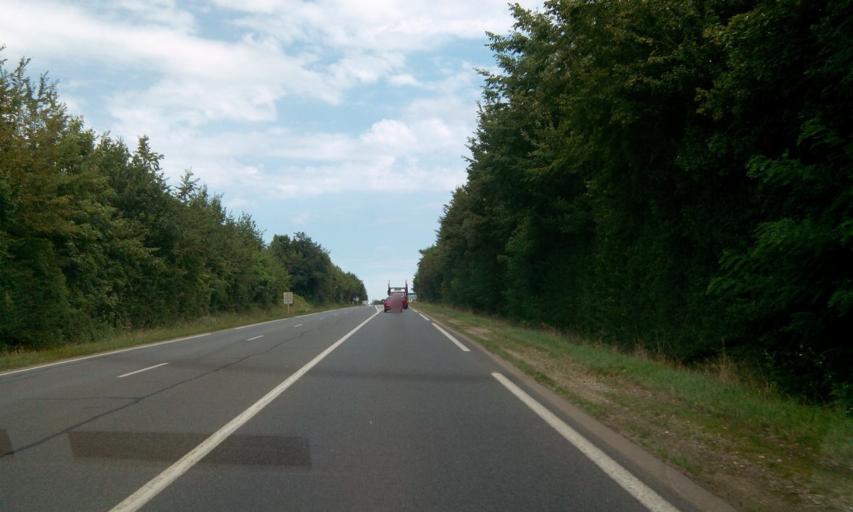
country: FR
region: Poitou-Charentes
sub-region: Departement des Deux-Sevres
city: Melle
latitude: 46.2175
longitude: -0.1569
